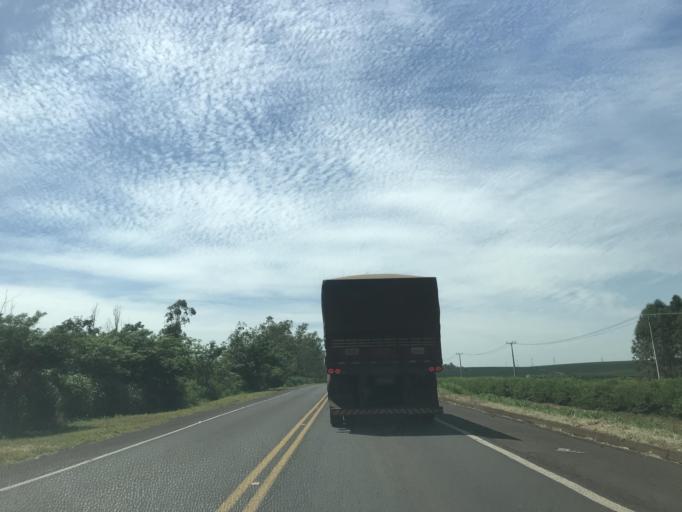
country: BR
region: Parana
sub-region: Paranavai
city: Nova Aurora
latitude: -22.9568
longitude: -52.6588
